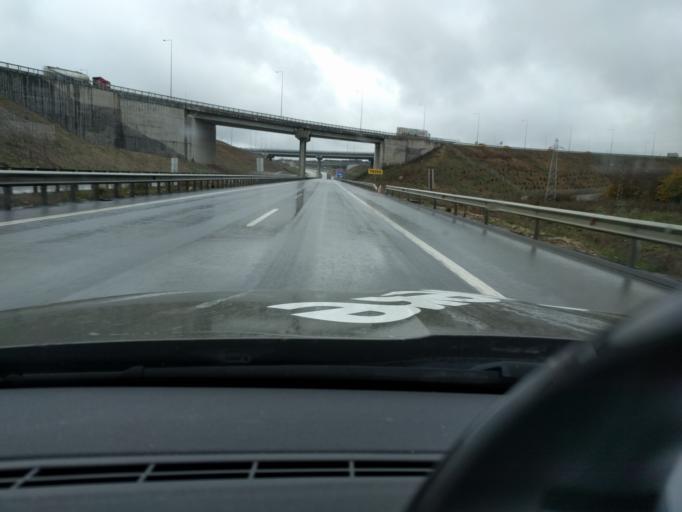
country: TR
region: Istanbul
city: Kemerburgaz
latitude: 41.2287
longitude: 28.8455
